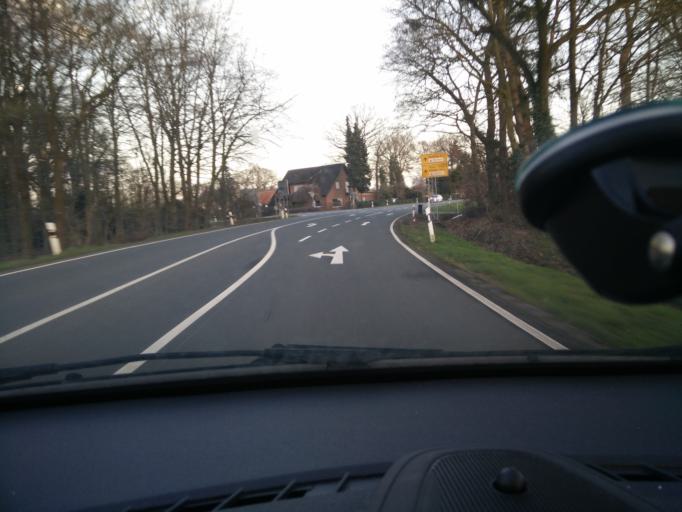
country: DE
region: North Rhine-Westphalia
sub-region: Regierungsbezirk Munster
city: Borken
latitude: 51.8090
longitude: 6.8862
